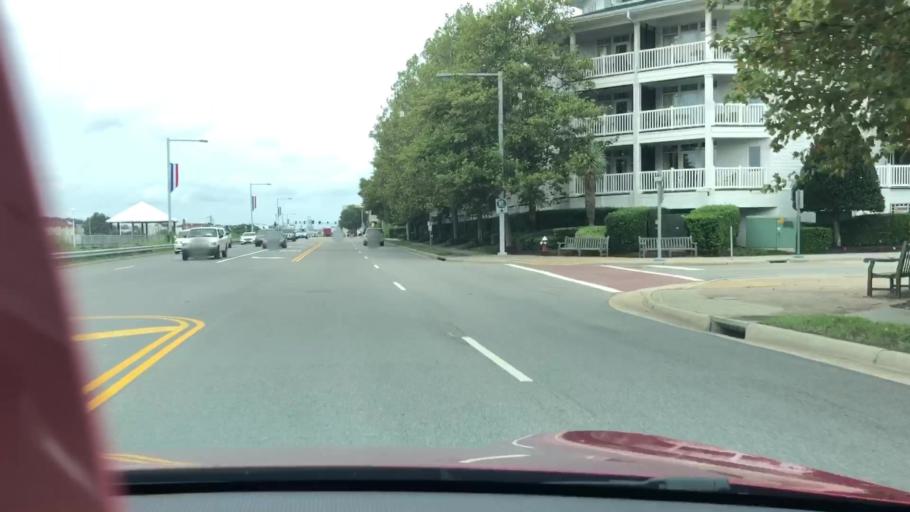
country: US
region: Virginia
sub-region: City of Virginia Beach
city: Virginia Beach
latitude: 36.8343
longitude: -75.9725
